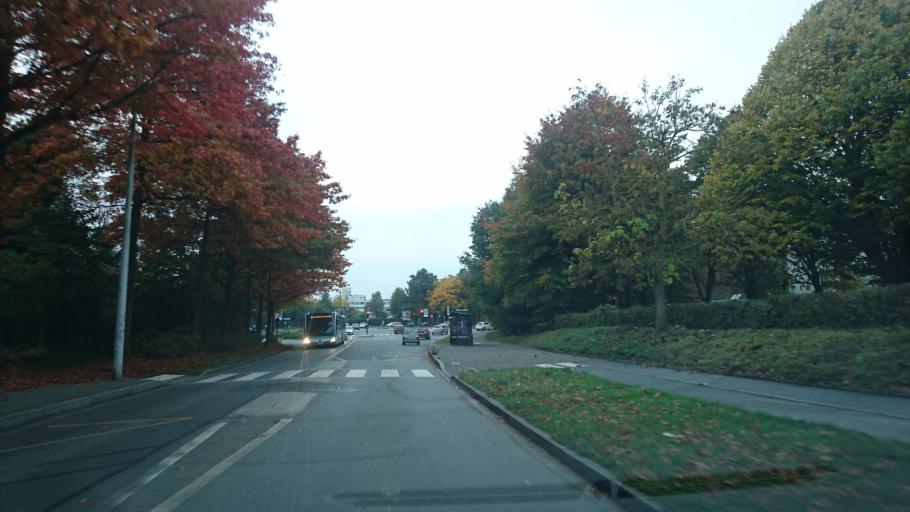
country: FR
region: Brittany
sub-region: Departement d'Ille-et-Vilaine
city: Saint-Gregoire
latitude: 48.1257
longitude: -1.7031
